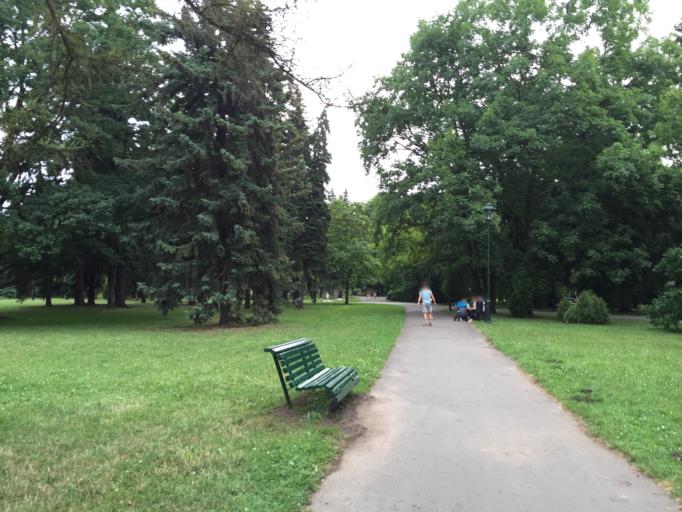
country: PL
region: Lesser Poland Voivodeship
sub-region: Krakow
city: Krakow
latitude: 50.0635
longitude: 19.9166
